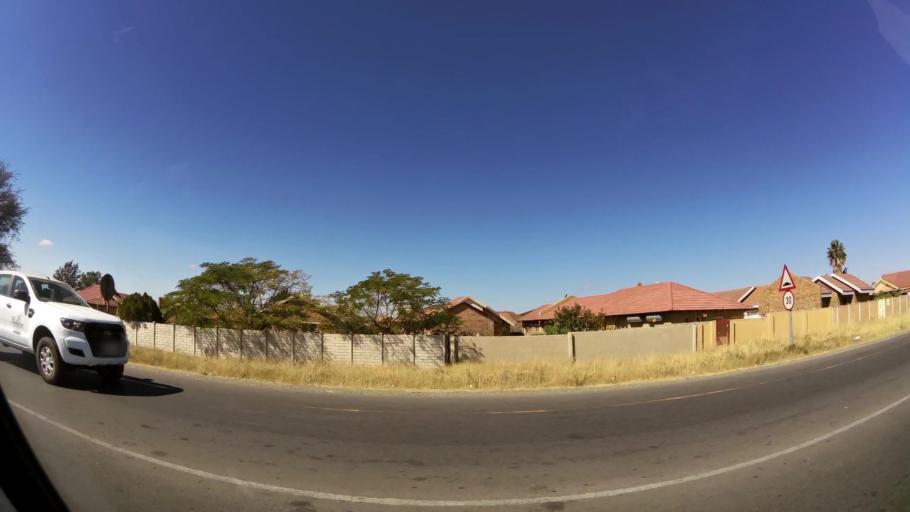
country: ZA
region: Limpopo
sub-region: Capricorn District Municipality
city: Polokwane
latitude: -23.8677
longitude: 29.4272
